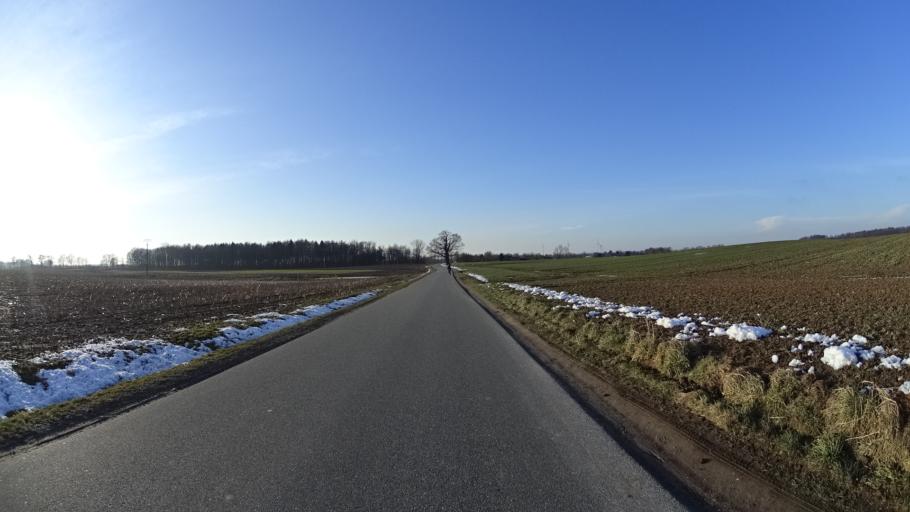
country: DE
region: Schleswig-Holstein
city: Fargau-Pratjau
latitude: 54.3352
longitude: 10.4126
